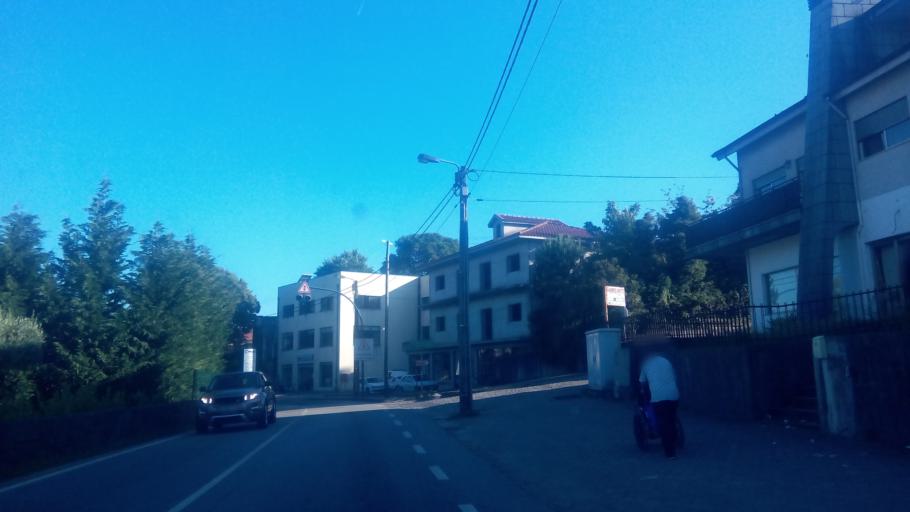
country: PT
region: Porto
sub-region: Paredes
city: Madalena
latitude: 41.2264
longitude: -8.3624
